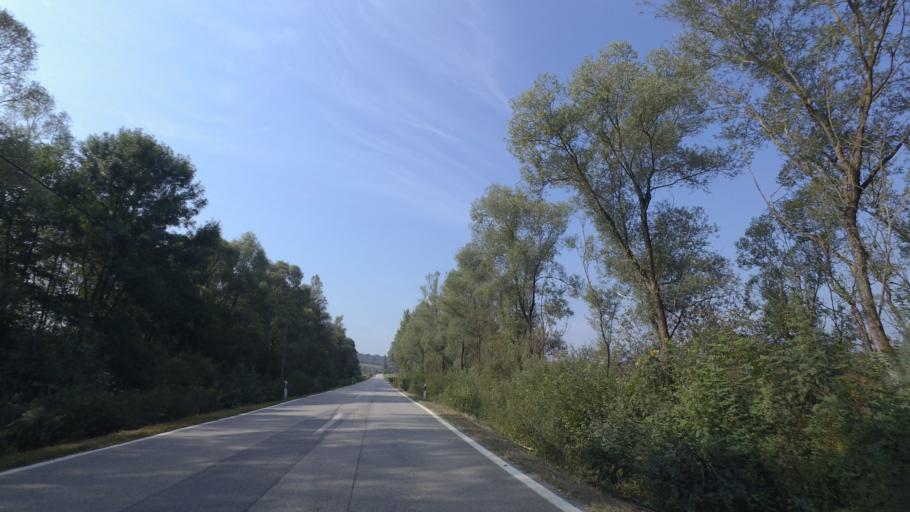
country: HR
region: Sisacko-Moslavacka
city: Novska
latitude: 45.3907
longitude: 17.0352
